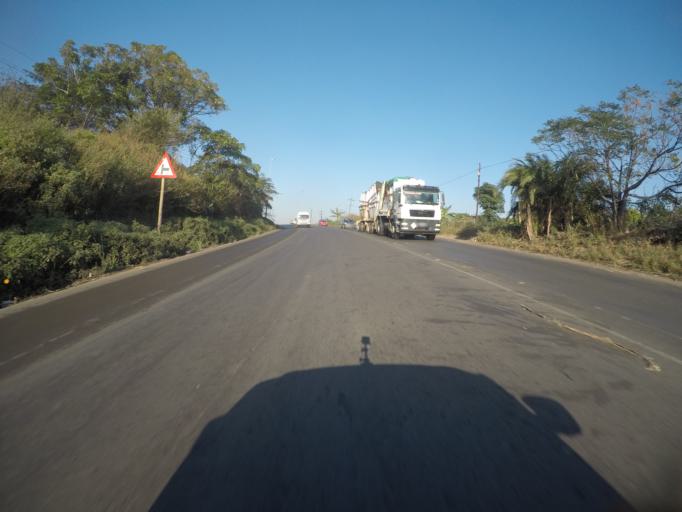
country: ZA
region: KwaZulu-Natal
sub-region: iLembe District Municipality
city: Stanger
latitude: -29.3878
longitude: 31.2515
